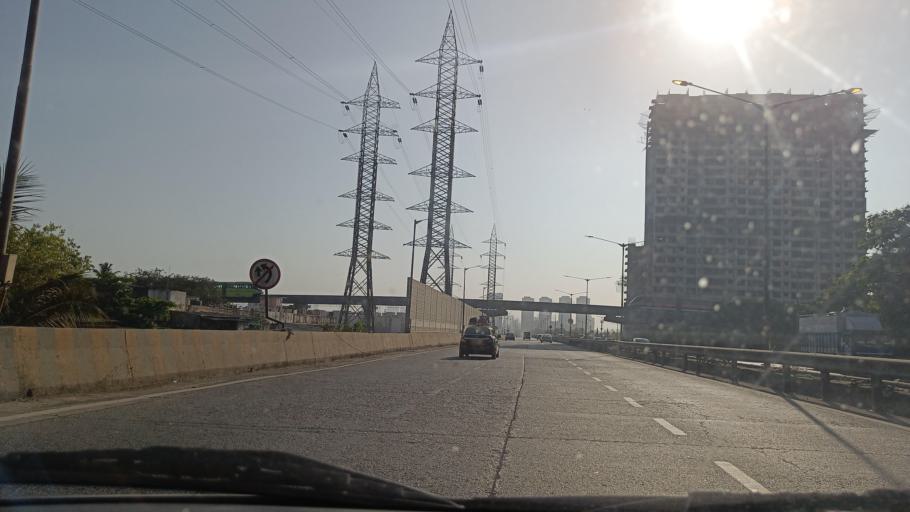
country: IN
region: Maharashtra
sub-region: Mumbai Suburban
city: Mumbai
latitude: 19.0334
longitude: 72.8978
